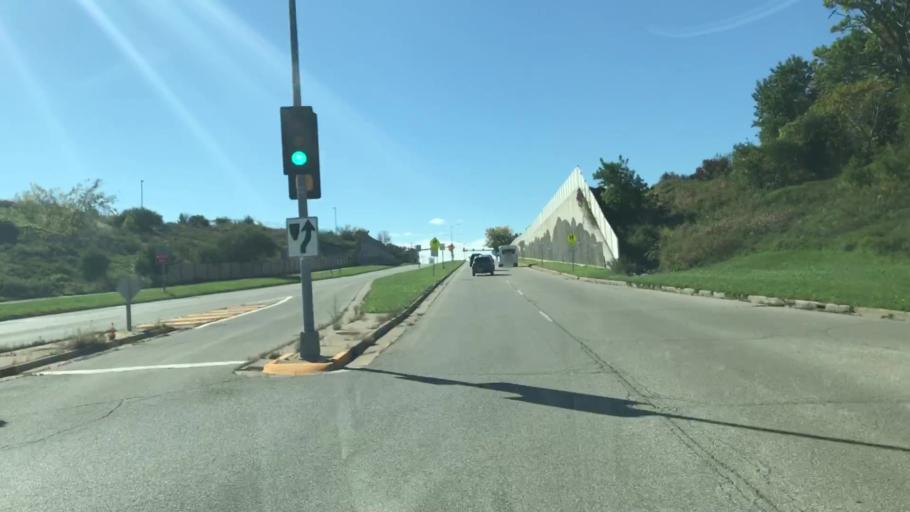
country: US
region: Wisconsin
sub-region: Waukesha County
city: Pewaukee
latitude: 43.0473
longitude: -88.2858
